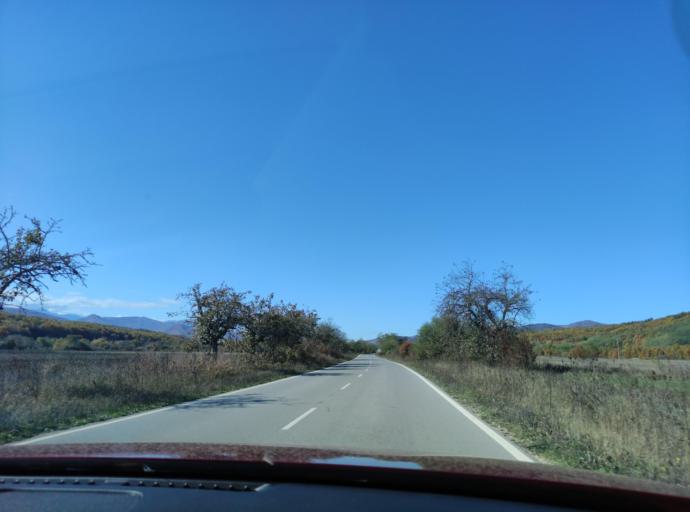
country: BG
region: Montana
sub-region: Obshtina Chiprovtsi
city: Chiprovtsi
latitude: 43.4105
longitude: 23.0473
